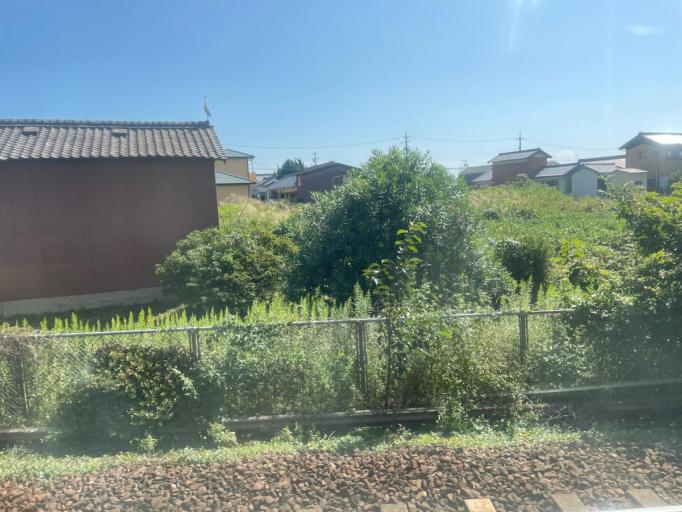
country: JP
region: Mie
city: Kawage
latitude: 34.8228
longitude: 136.5780
